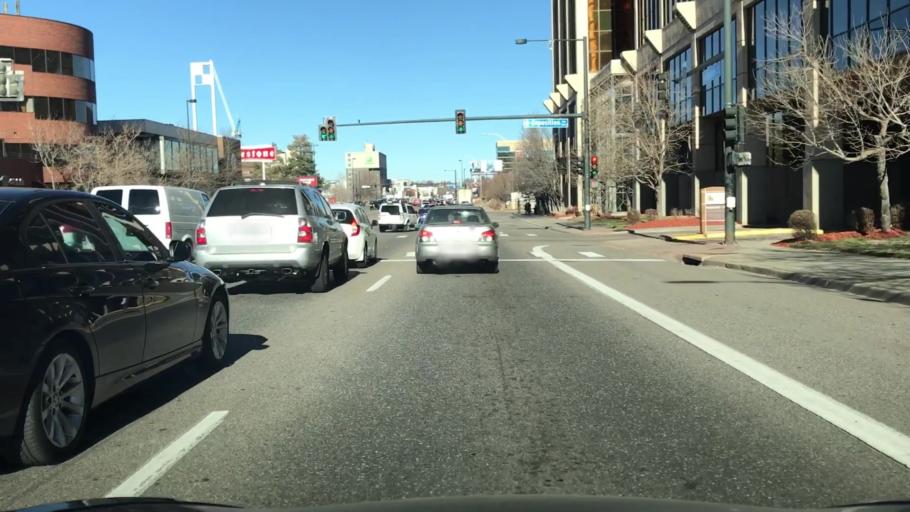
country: US
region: Colorado
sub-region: Arapahoe County
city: Glendale
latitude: 39.7035
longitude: -104.9406
